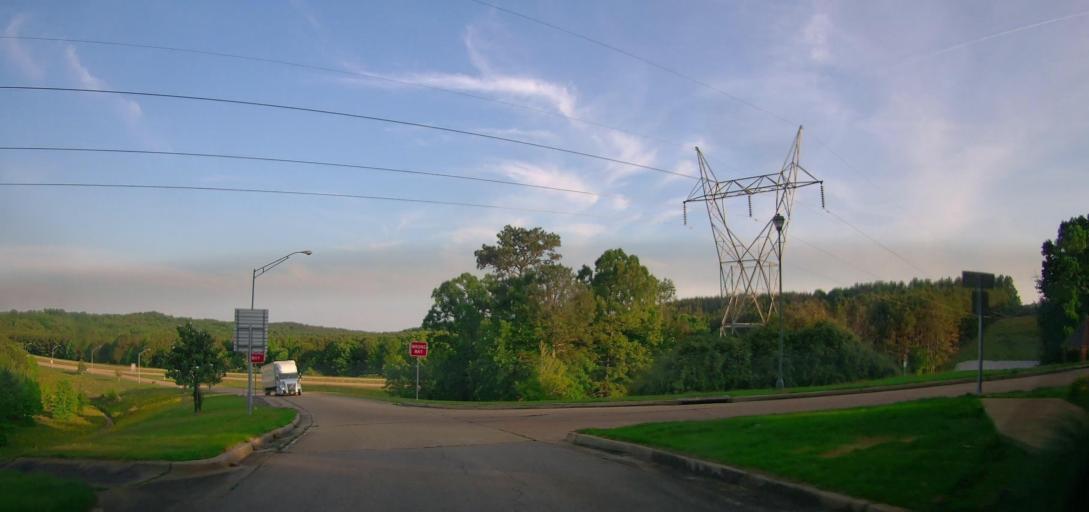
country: US
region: Mississippi
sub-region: Itawamba County
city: Fulton
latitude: 34.2217
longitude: -88.2321
